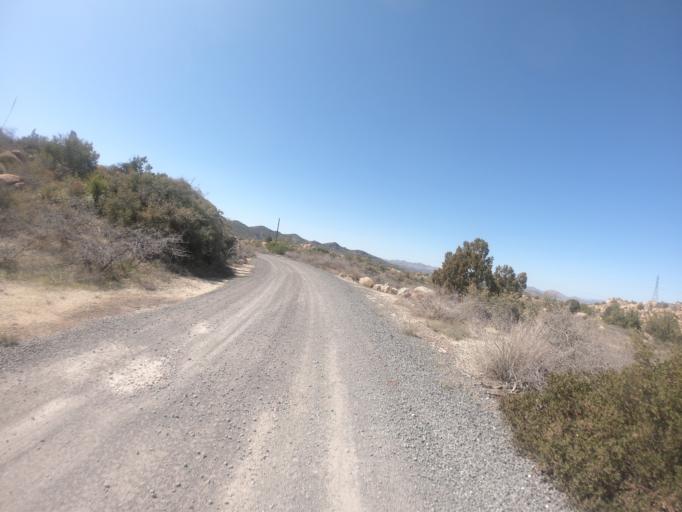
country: US
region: Arizona
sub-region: Gila County
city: Miami
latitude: 33.3571
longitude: -110.9709
